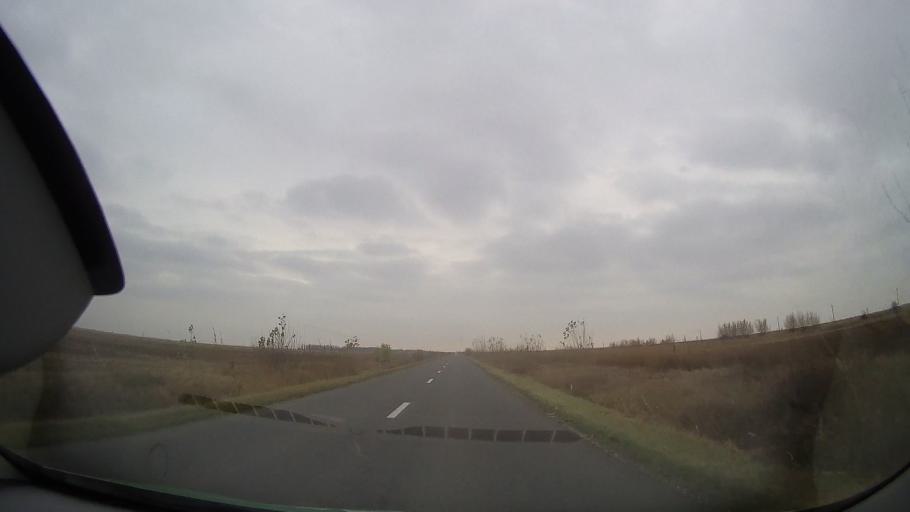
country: RO
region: Ialomita
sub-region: Comuna Garbovi
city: Garbovi
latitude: 44.7488
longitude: 26.7186
